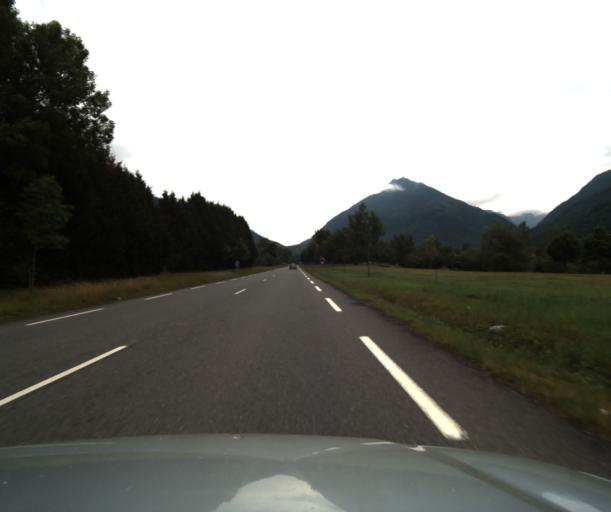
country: FR
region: Midi-Pyrenees
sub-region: Departement des Hautes-Pyrenees
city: Pierrefitte-Nestalas
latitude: 42.9832
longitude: -0.0712
